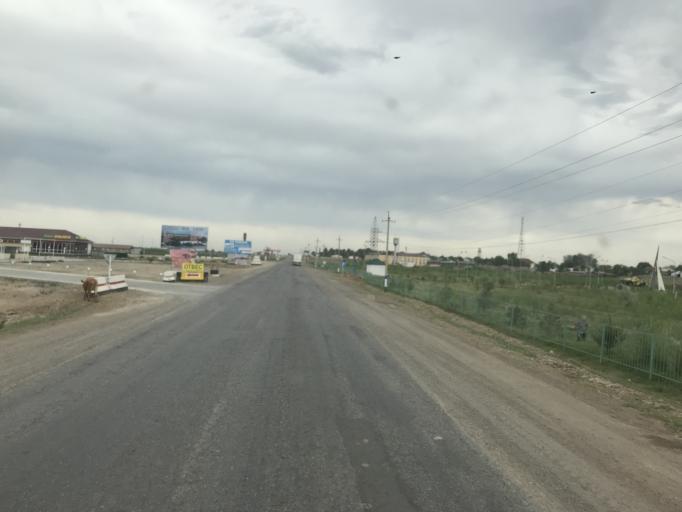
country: KZ
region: Ongtustik Qazaqstan
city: Asykata
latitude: 40.9630
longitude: 68.4597
